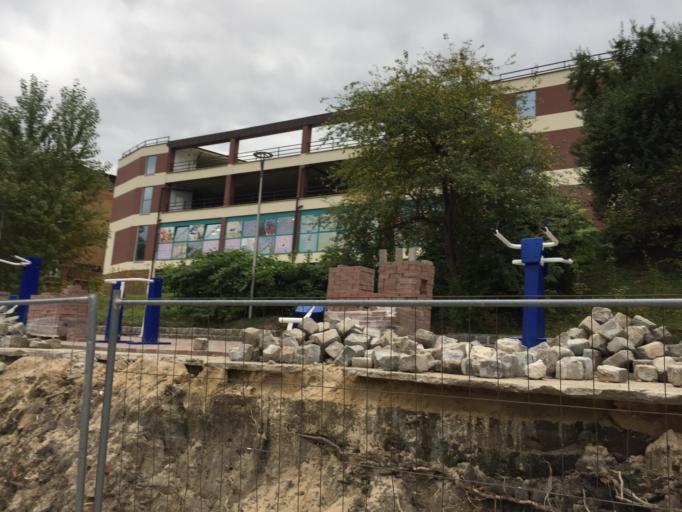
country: RU
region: Kaliningrad
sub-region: Gorod Kaliningrad
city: Kaliningrad
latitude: 54.7176
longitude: 20.5204
